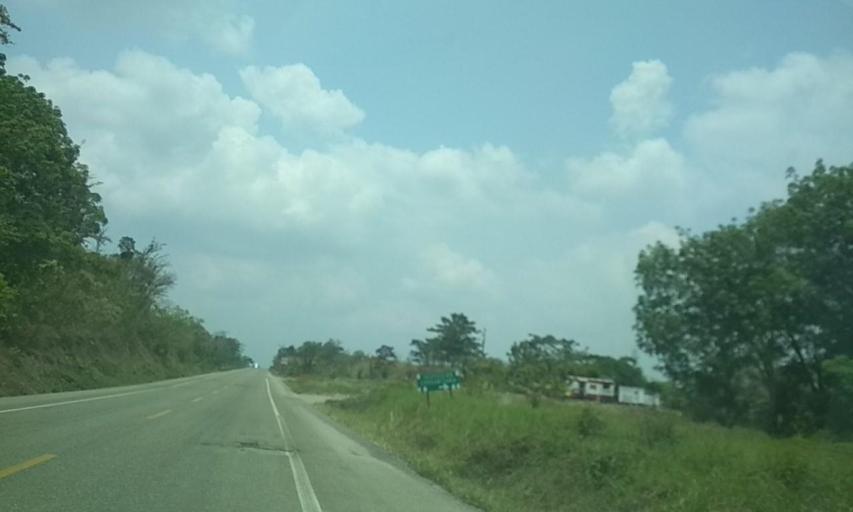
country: MX
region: Tabasco
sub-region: Huimanguillo
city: Francisco Rueda
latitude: 17.6440
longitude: -93.8246
